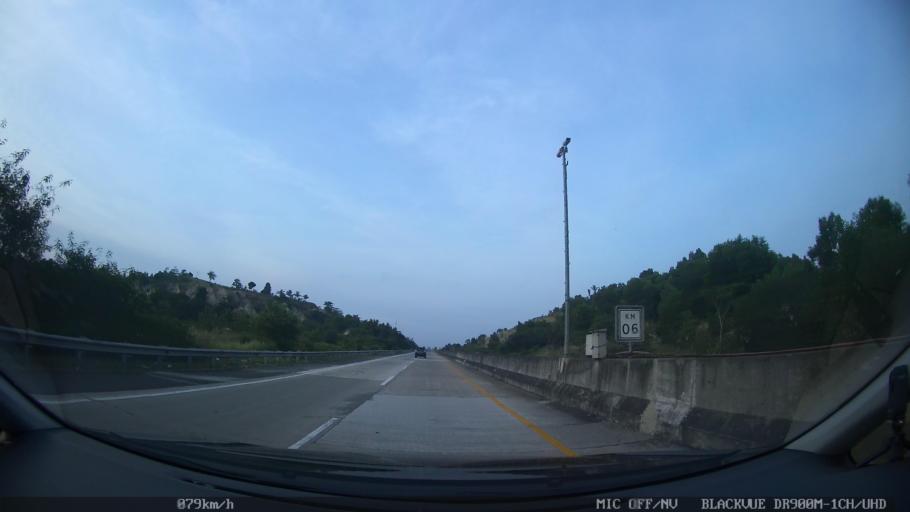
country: ID
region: Lampung
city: Penengahan
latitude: -5.8299
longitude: 105.7327
